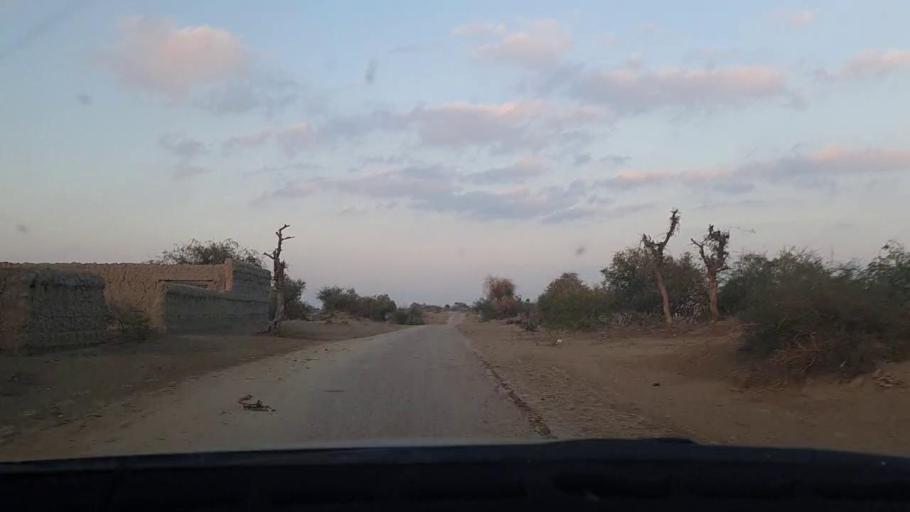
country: PK
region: Sindh
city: Tando Mittha Khan
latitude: 25.9583
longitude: 69.3426
